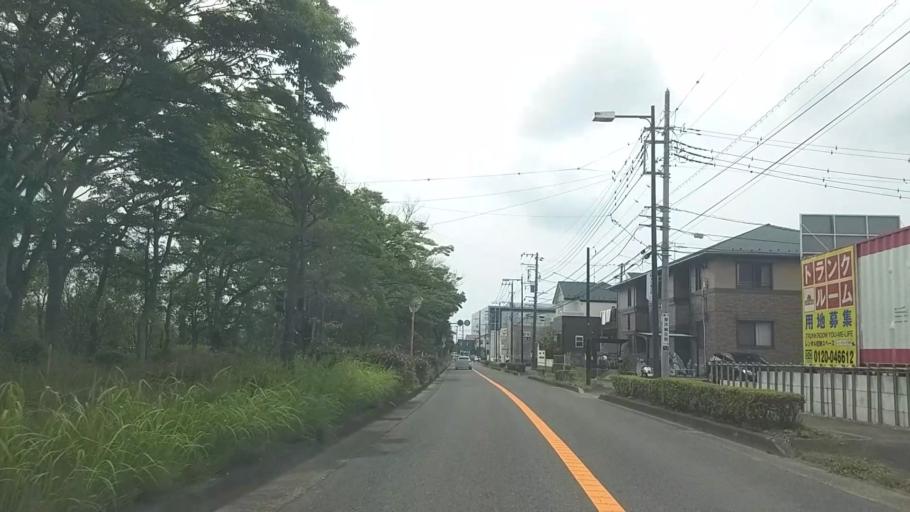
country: JP
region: Kanagawa
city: Fujisawa
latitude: 35.3449
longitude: 139.4665
